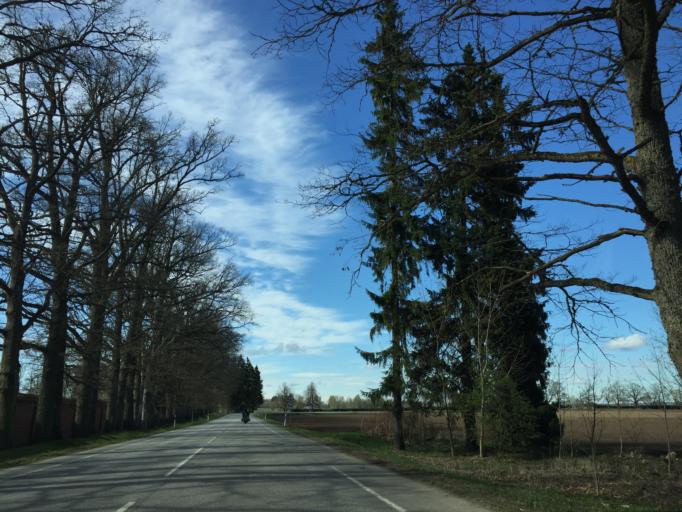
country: EE
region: Vorumaa
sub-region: Antsla vald
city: Vana-Antsla
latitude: 57.9015
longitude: 26.2869
